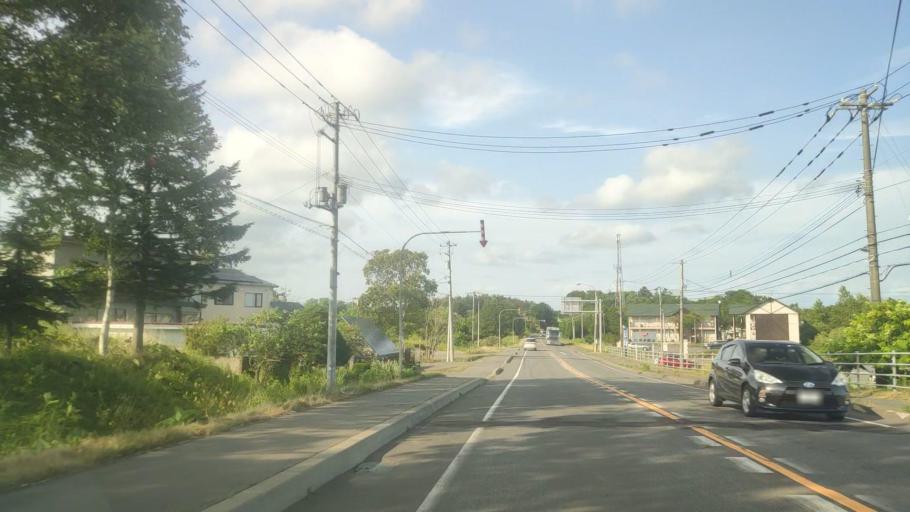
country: JP
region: Hokkaido
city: Chitose
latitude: 42.7322
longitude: 141.7751
